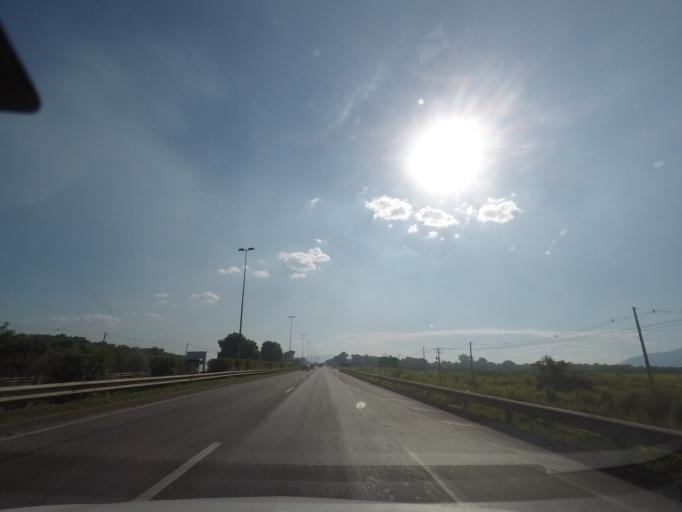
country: BR
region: Rio de Janeiro
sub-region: Duque De Caxias
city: Duque de Caxias
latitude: -22.6573
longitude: -43.2475
